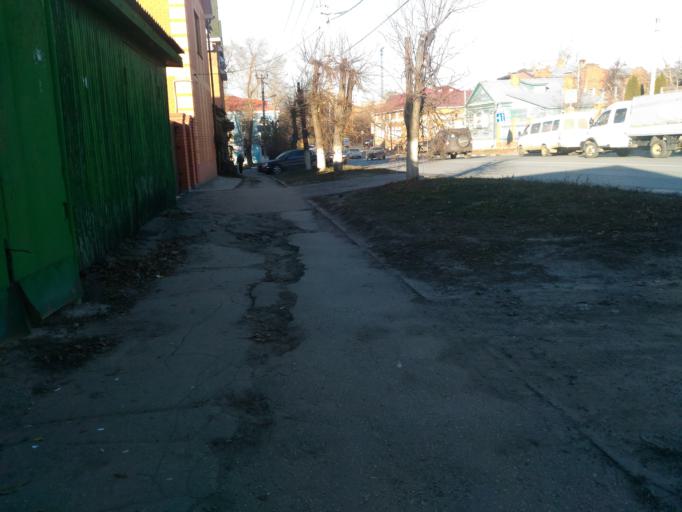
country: RU
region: Ulyanovsk
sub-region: Ulyanovskiy Rayon
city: Ulyanovsk
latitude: 54.3118
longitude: 48.3785
